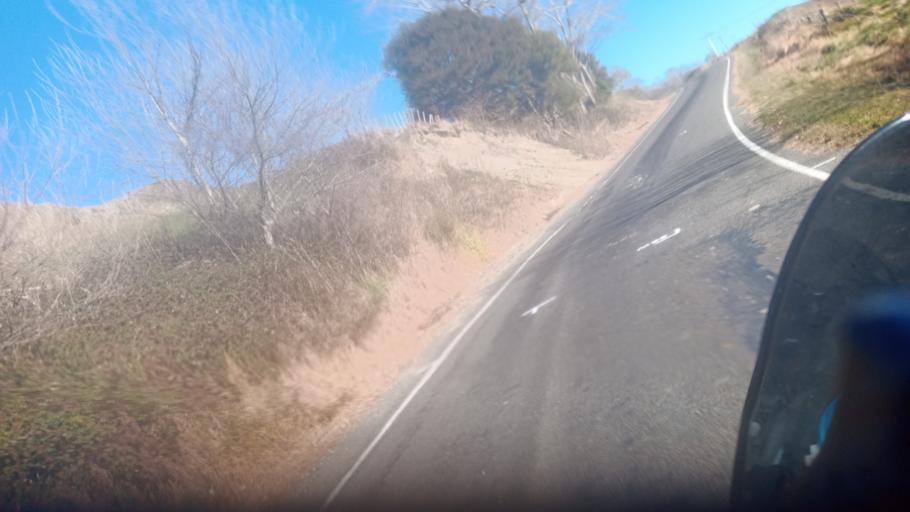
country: NZ
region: Gisborne
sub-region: Gisborne District
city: Gisborne
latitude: -38.5760
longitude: 177.5788
